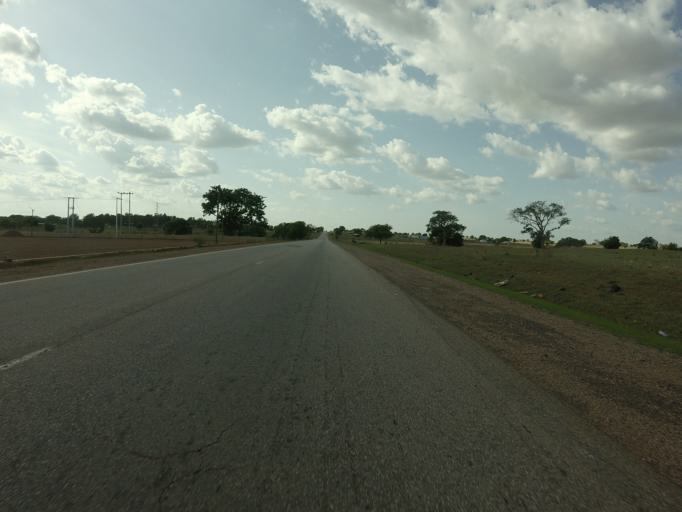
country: GH
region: Upper East
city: Bolgatanga
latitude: 10.6701
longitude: -0.8606
